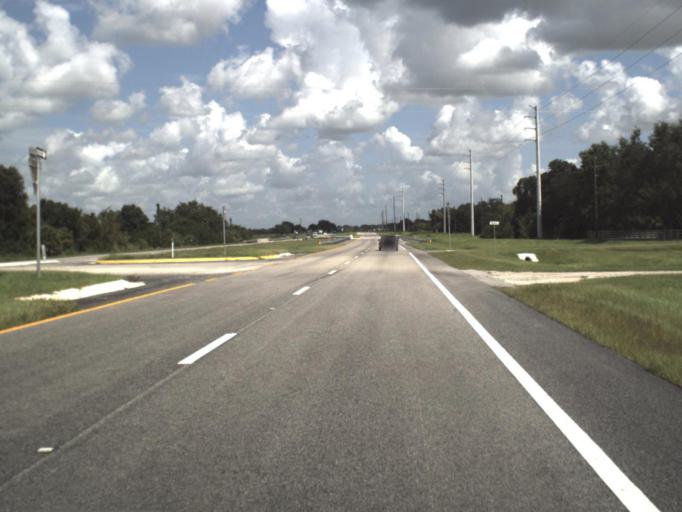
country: US
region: Florida
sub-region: Charlotte County
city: Harbour Heights
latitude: 27.0621
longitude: -81.9581
